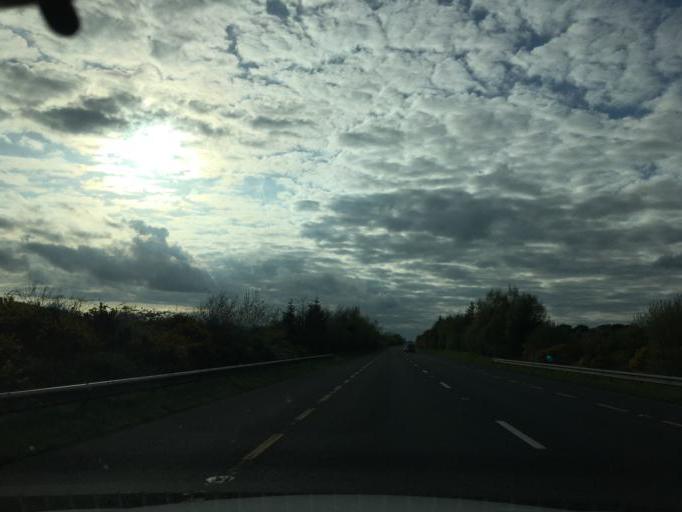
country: IE
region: Leinster
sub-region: Loch Garman
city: Enniscorthy
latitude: 52.3567
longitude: -6.6968
